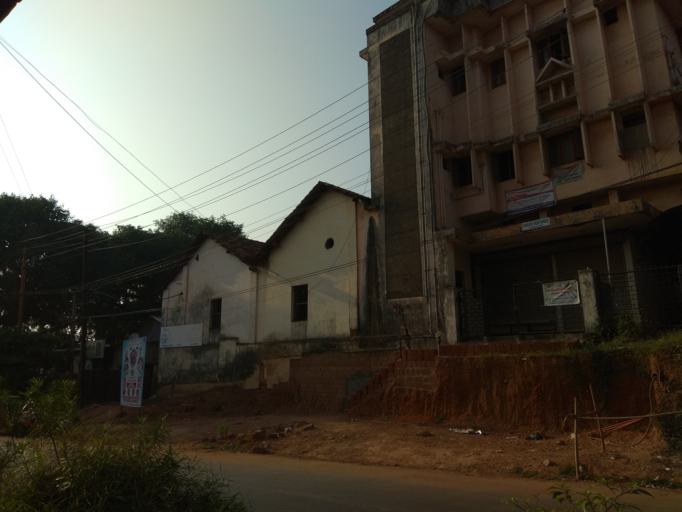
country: IN
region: Karnataka
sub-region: Dakshina Kannada
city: Mangalore
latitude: 12.9072
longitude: 74.8491
